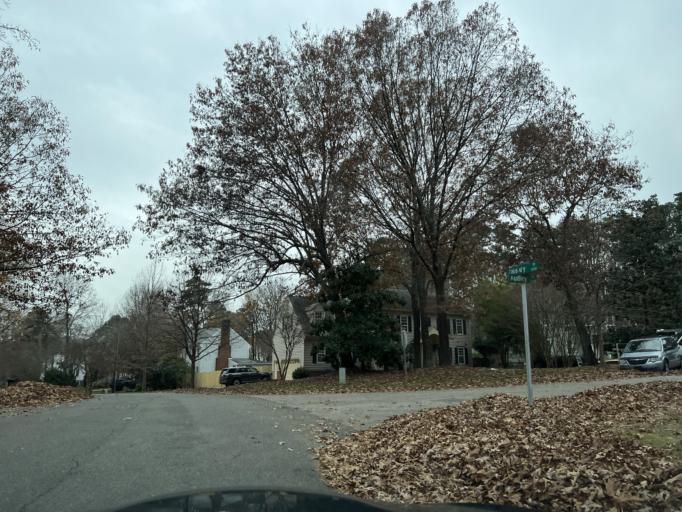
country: US
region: North Carolina
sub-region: Wake County
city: Wake Forest
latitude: 35.8974
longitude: -78.6020
